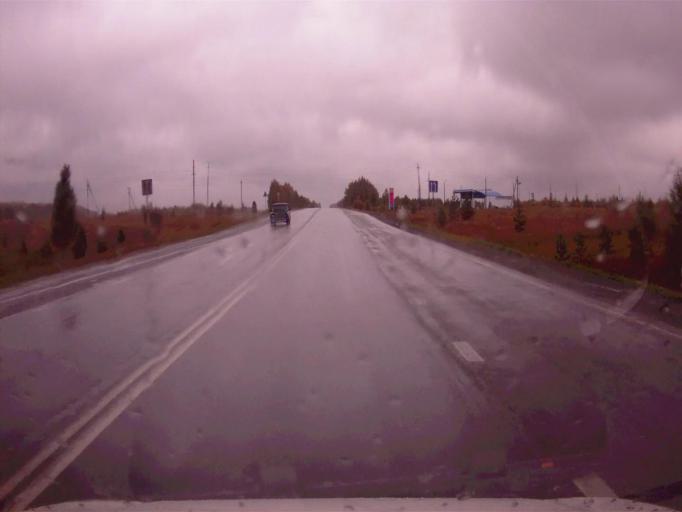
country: RU
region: Chelyabinsk
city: Argayash
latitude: 55.4777
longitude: 60.8548
